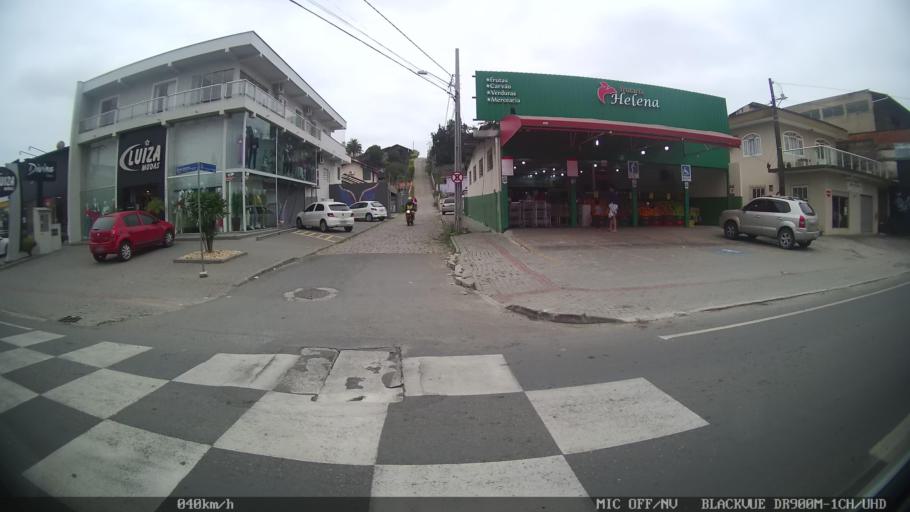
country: BR
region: Santa Catarina
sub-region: Joinville
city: Joinville
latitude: -26.3355
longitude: -48.8476
